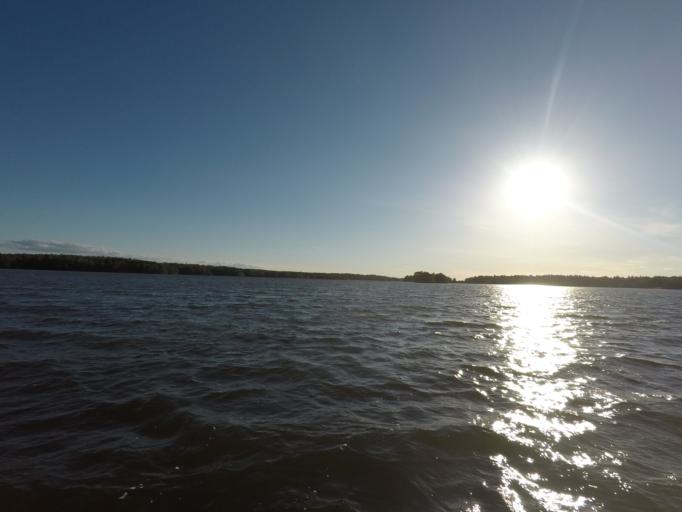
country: SE
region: Soedermanland
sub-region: Eskilstuna Kommun
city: Kvicksund
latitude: 59.4594
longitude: 16.3874
